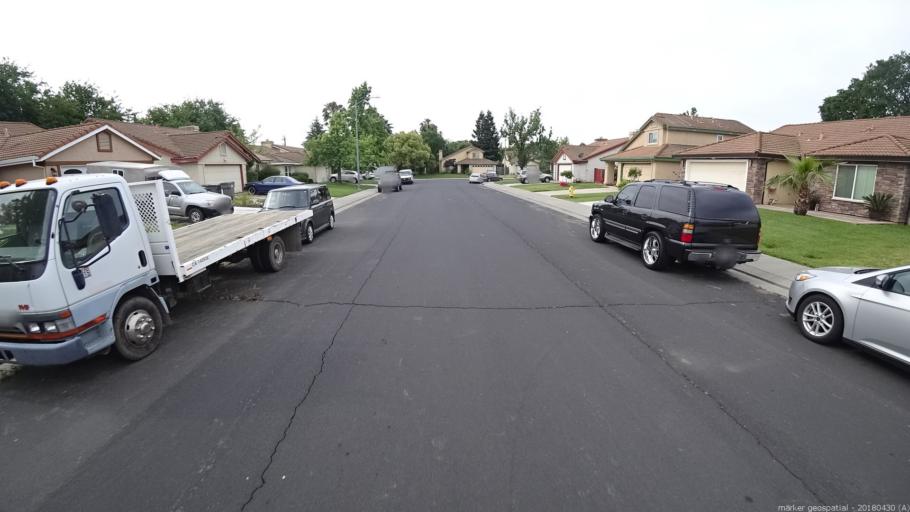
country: US
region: California
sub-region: Yolo County
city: West Sacramento
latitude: 38.5913
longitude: -121.5318
